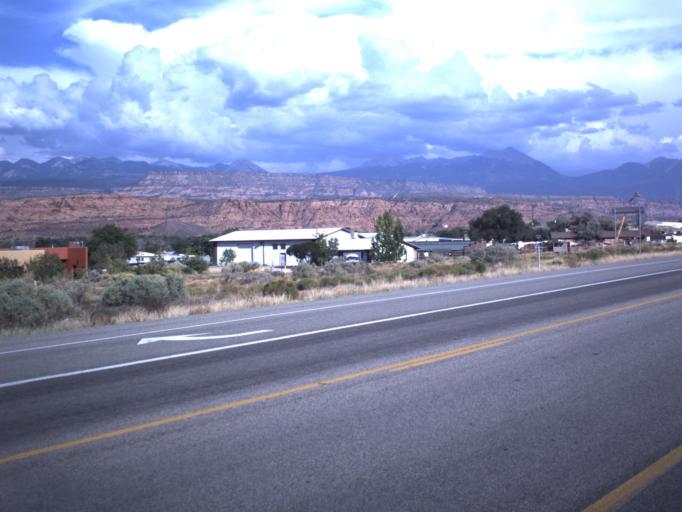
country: US
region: Utah
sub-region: Grand County
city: Moab
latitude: 38.5280
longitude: -109.5032
